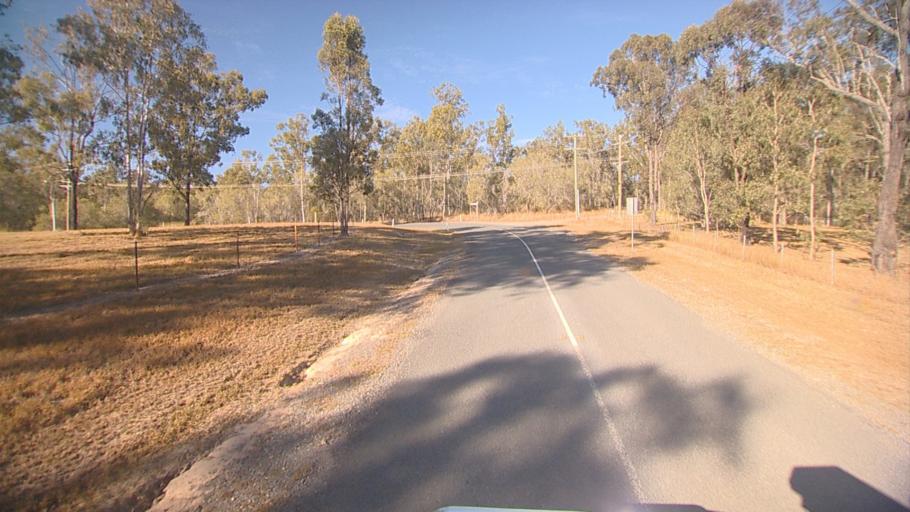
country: AU
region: Queensland
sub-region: Logan
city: Cedar Vale
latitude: -27.8449
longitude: 153.0821
